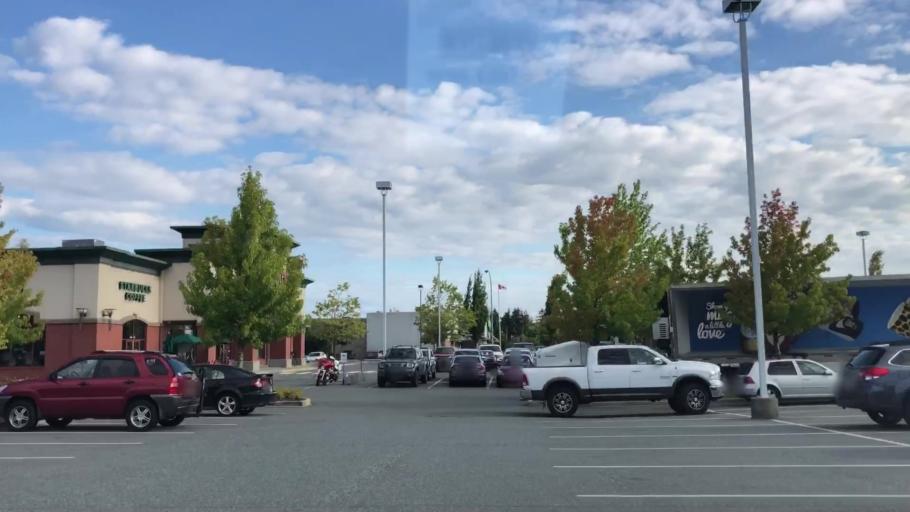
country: CA
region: British Columbia
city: Nanaimo
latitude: 49.2376
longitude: -124.0541
